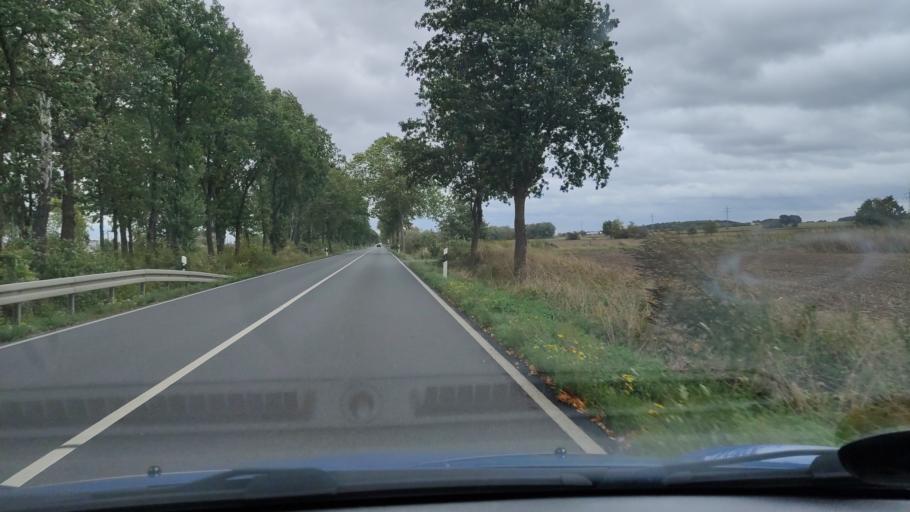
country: DE
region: Lower Saxony
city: Seelze
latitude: 52.3889
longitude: 9.6171
